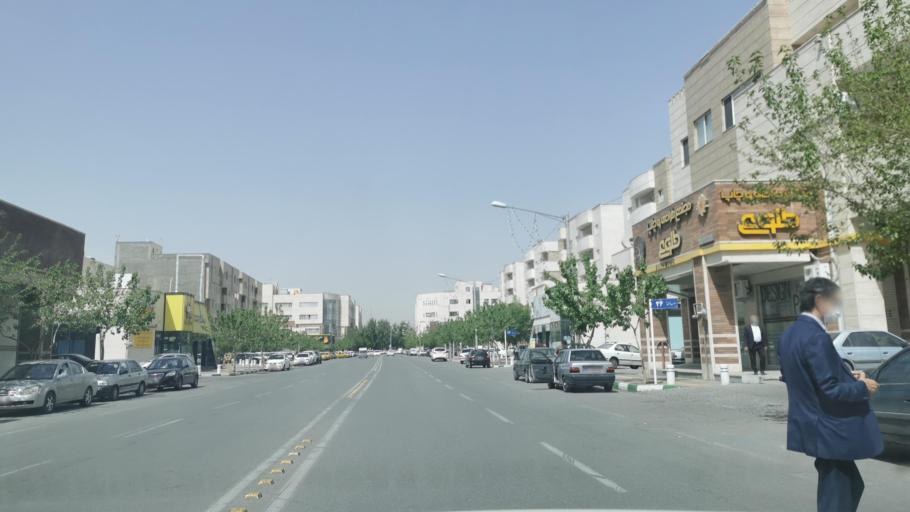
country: IR
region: Razavi Khorasan
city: Mashhad
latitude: 36.3020
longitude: 59.6267
